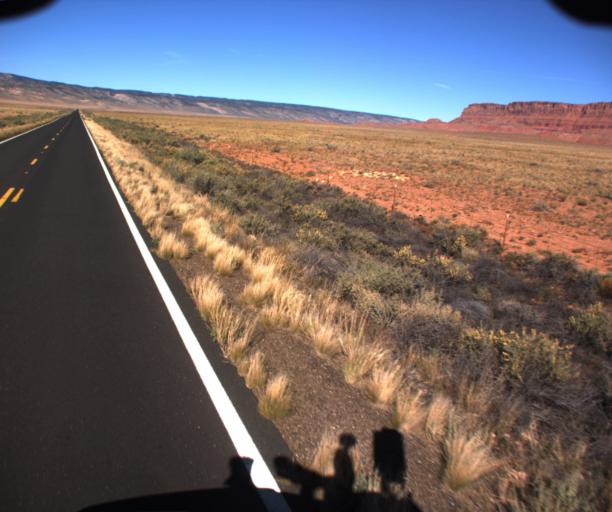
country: US
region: Arizona
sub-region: Coconino County
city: Page
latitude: 36.7091
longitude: -111.9649
